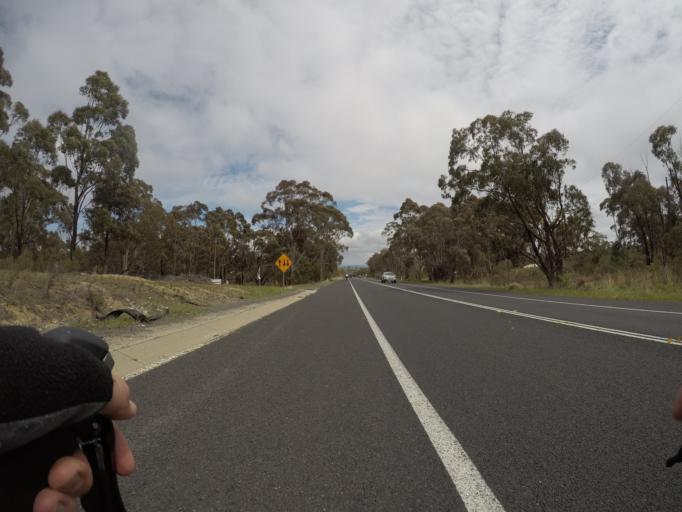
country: AU
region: New South Wales
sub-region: Bathurst Regional
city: Kelso
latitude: -33.4522
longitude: 149.7912
